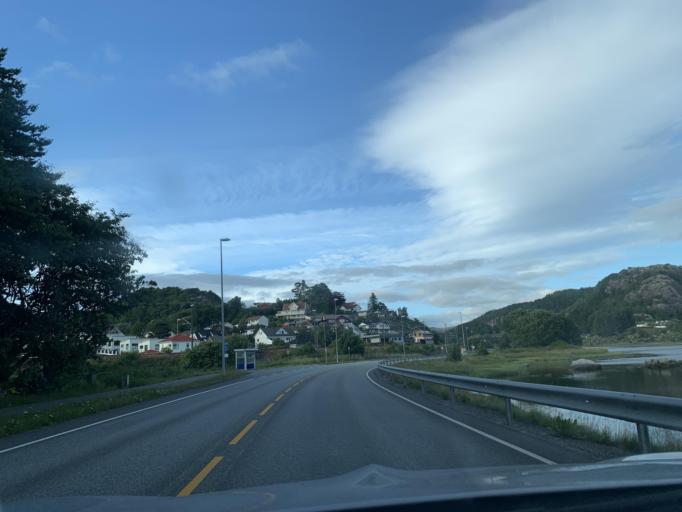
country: NO
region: Rogaland
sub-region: Eigersund
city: Egersund
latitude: 58.4620
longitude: 6.0172
